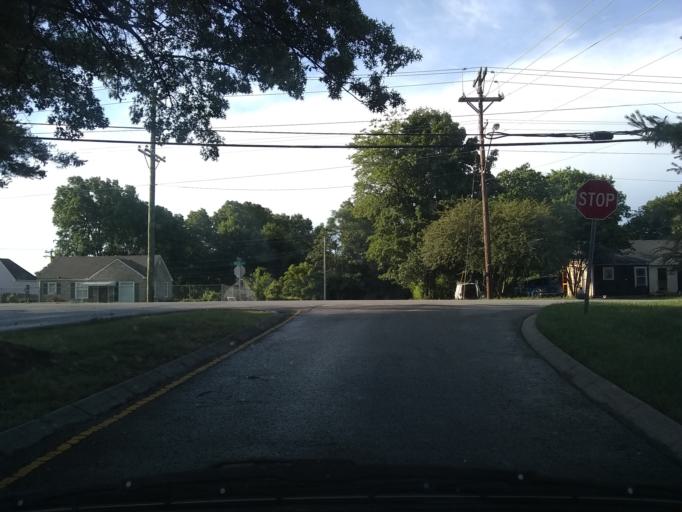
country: US
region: Tennessee
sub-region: Davidson County
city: Oak Hill
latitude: 36.1235
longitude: -86.7038
